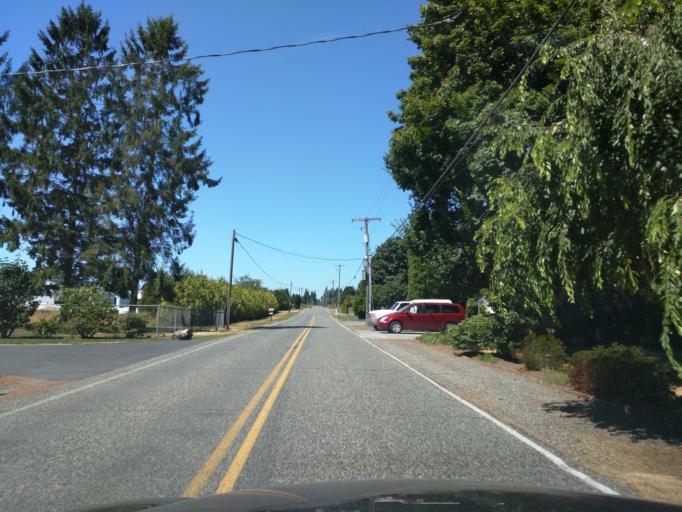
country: US
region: Washington
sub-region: Whatcom County
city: Lynden
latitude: 48.8844
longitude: -122.4510
